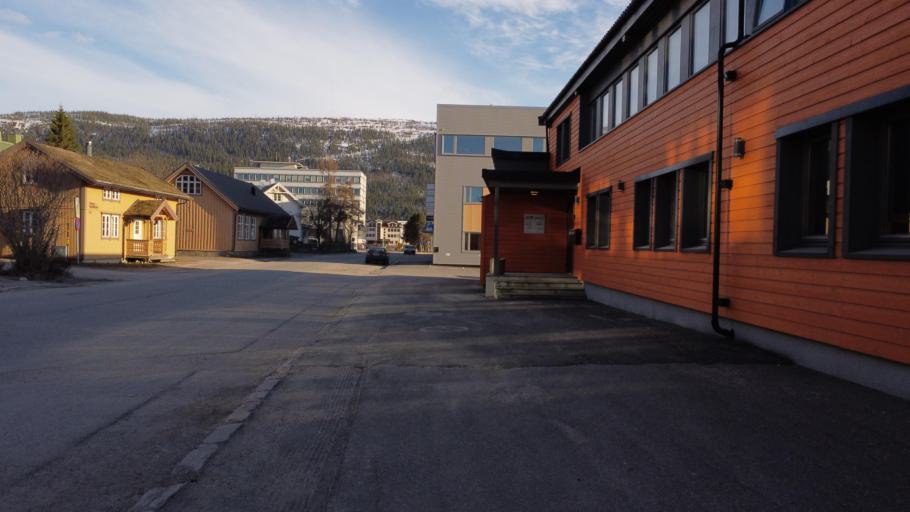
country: NO
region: Nordland
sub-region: Rana
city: Mo i Rana
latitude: 66.3137
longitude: 14.1322
